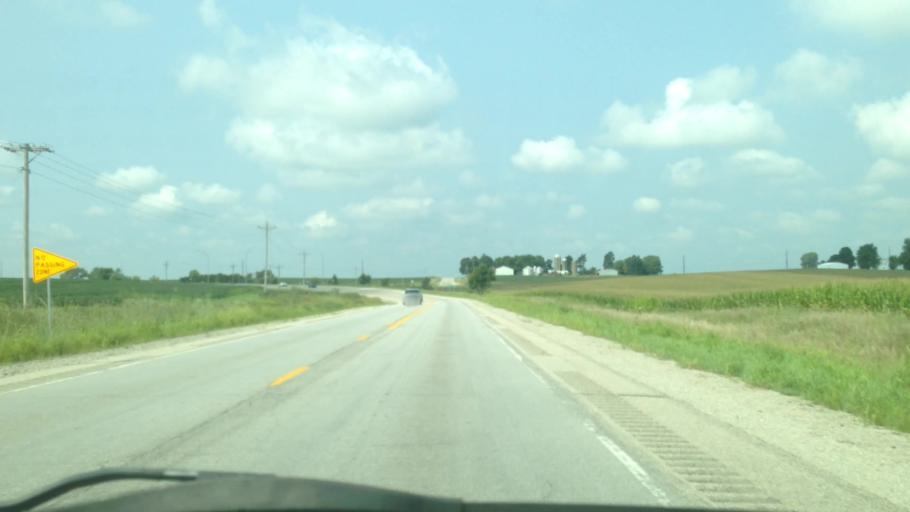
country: US
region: Iowa
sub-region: Benton County
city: Walford
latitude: 41.8762
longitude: -91.8627
